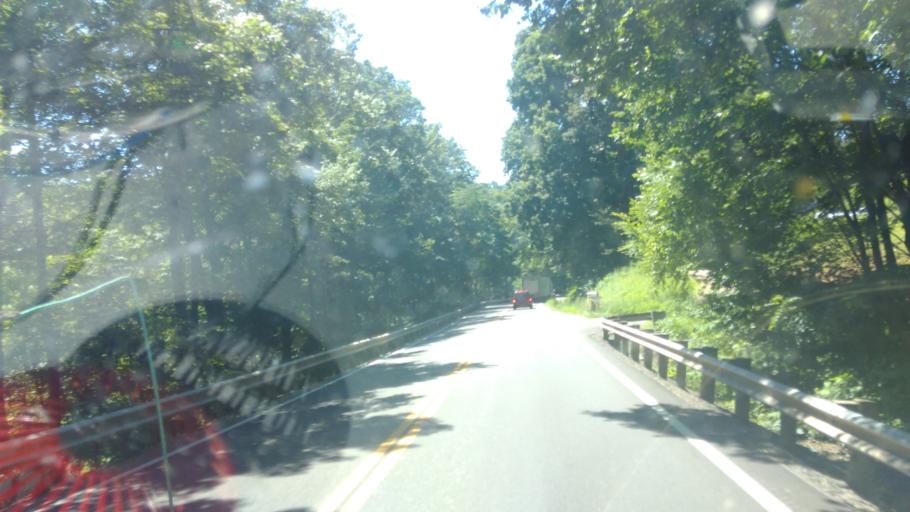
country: US
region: Ohio
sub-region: Carroll County
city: Carrollton
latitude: 40.4977
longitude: -80.9747
